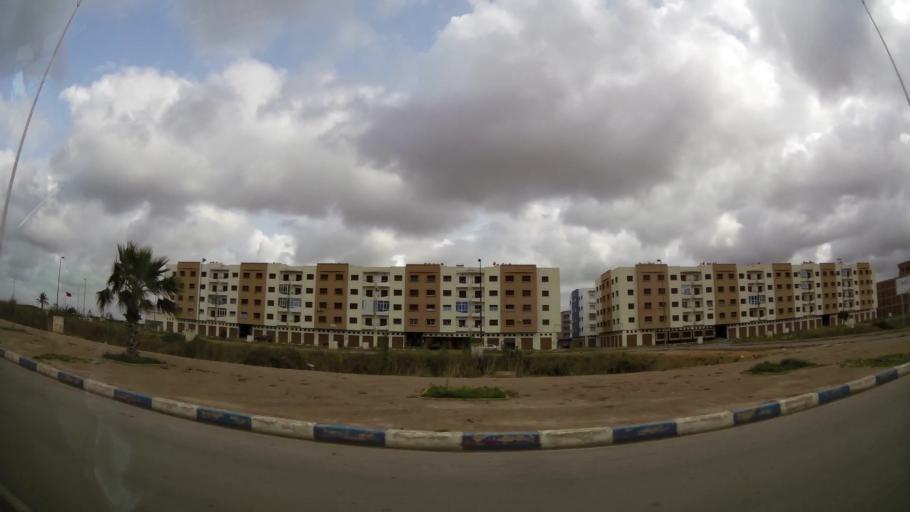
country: MA
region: Oriental
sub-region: Nador
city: Nador
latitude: 35.1537
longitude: -2.9088
